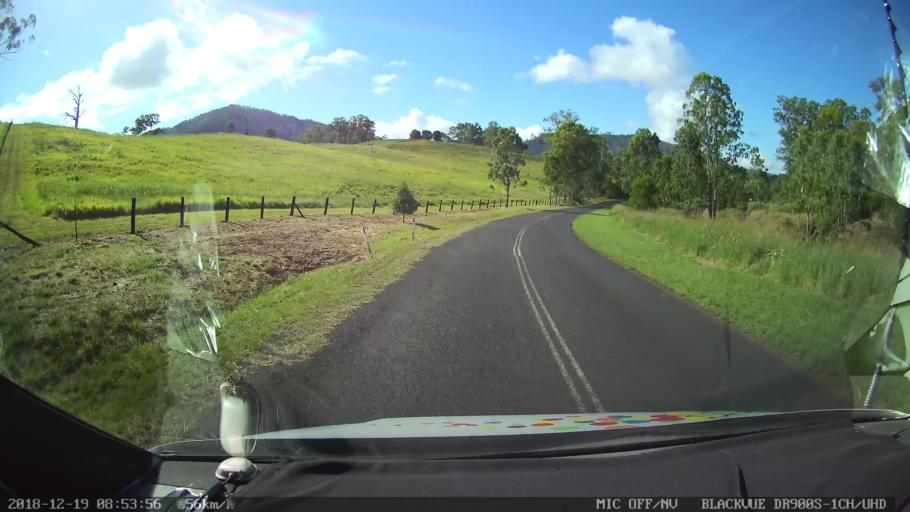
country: AU
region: New South Wales
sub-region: Kyogle
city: Kyogle
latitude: -28.4060
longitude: 152.9797
